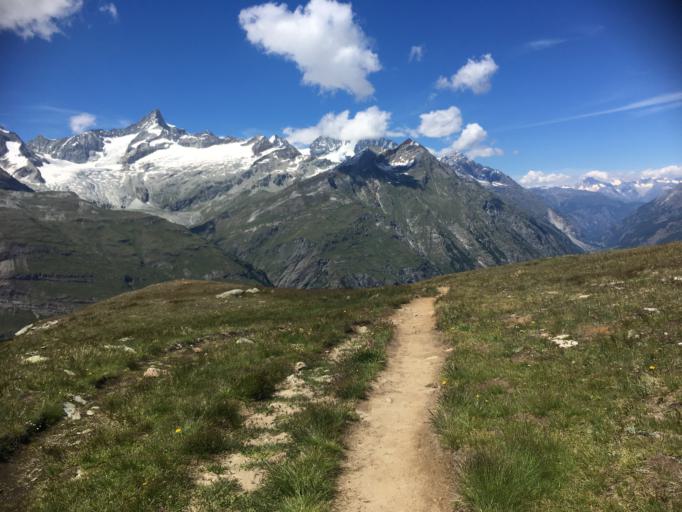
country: CH
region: Valais
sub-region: Visp District
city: Zermatt
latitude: 45.9894
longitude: 7.7523
